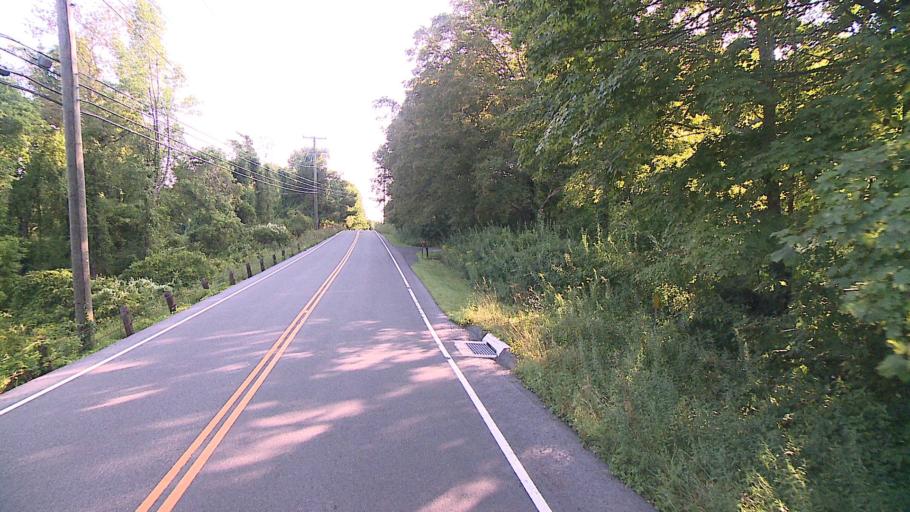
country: US
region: Connecticut
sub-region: Litchfield County
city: Kent
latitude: 41.7582
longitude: -73.4379
